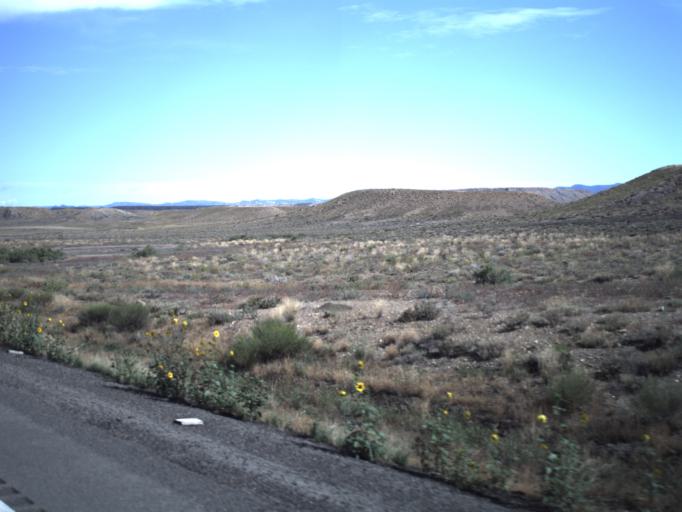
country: US
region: Utah
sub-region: Carbon County
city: East Carbon City
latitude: 39.4574
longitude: -110.4831
